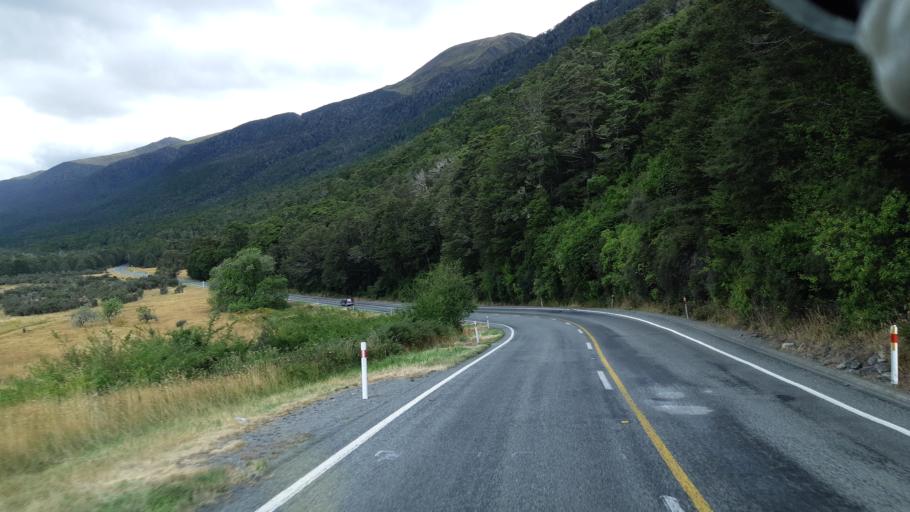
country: NZ
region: Canterbury
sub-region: Hurunui District
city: Amberley
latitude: -42.4750
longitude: 172.3942
